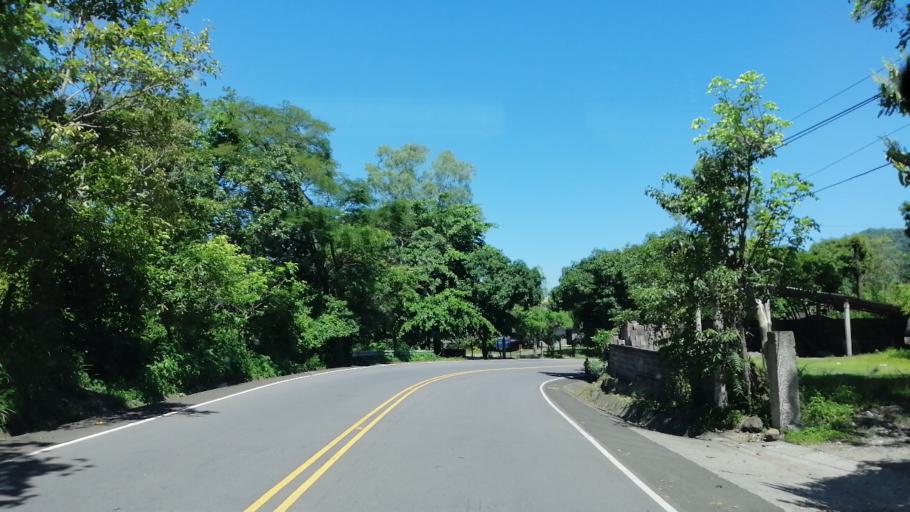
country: SV
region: Morazan
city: Cacaopera
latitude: 13.8136
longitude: -88.1704
